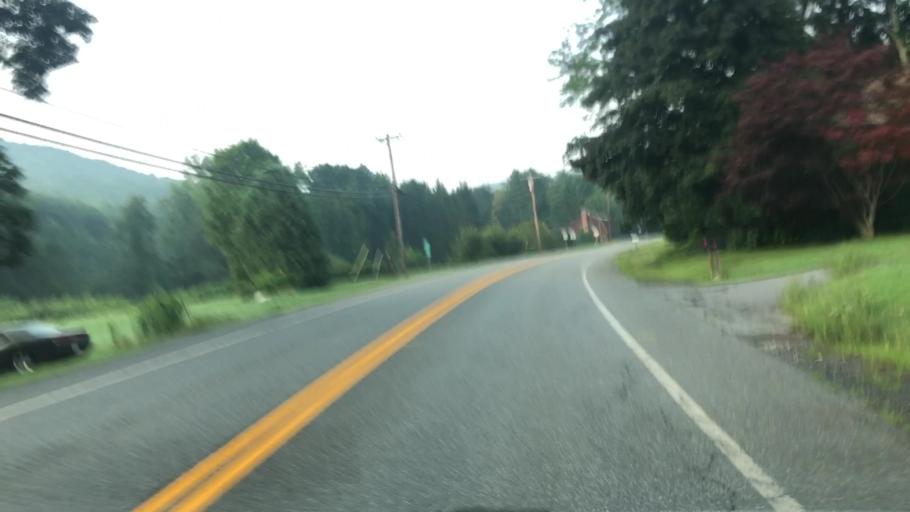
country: US
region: Massachusetts
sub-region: Franklin County
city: Buckland
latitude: 42.5664
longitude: -72.8023
